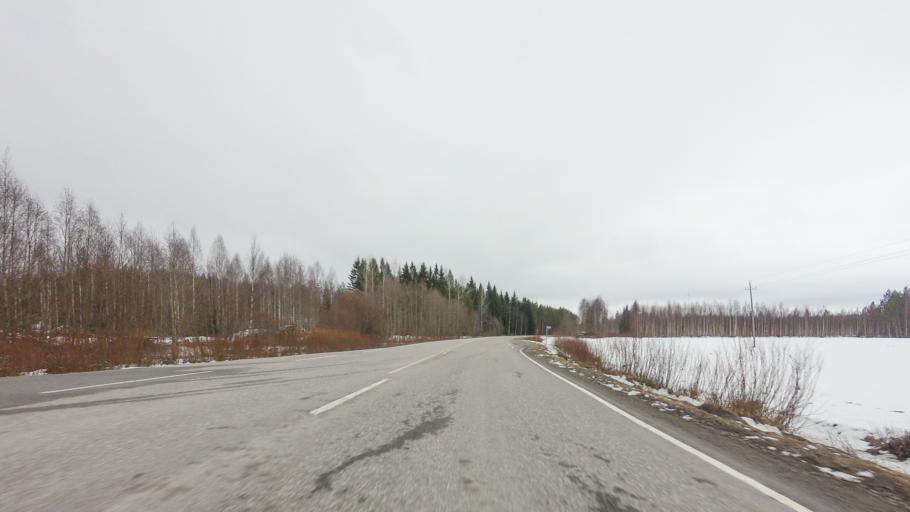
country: FI
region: Southern Savonia
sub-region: Savonlinna
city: Savonlinna
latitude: 61.9071
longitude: 28.9281
